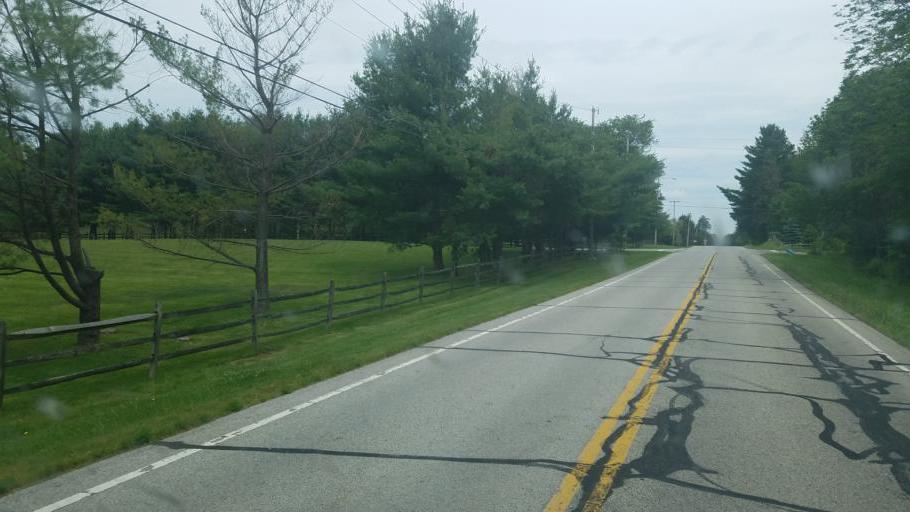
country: US
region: Ohio
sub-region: Geauga County
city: Bainbridge
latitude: 41.4091
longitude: -81.2477
